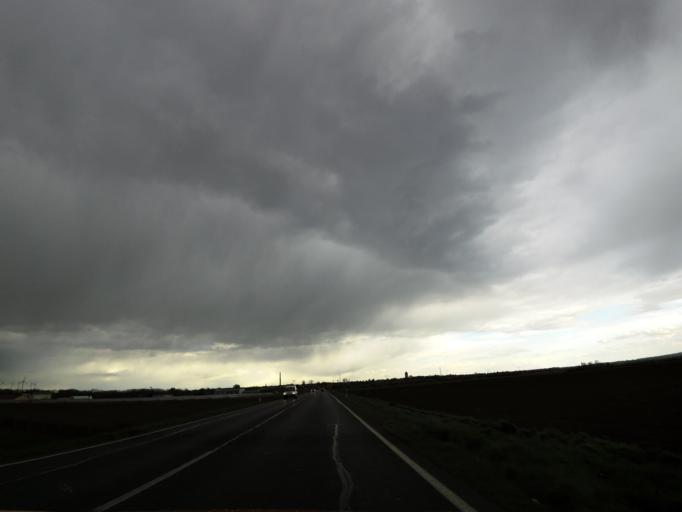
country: DE
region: Saxony-Anhalt
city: Westeregeln
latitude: 51.9407
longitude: 11.3981
